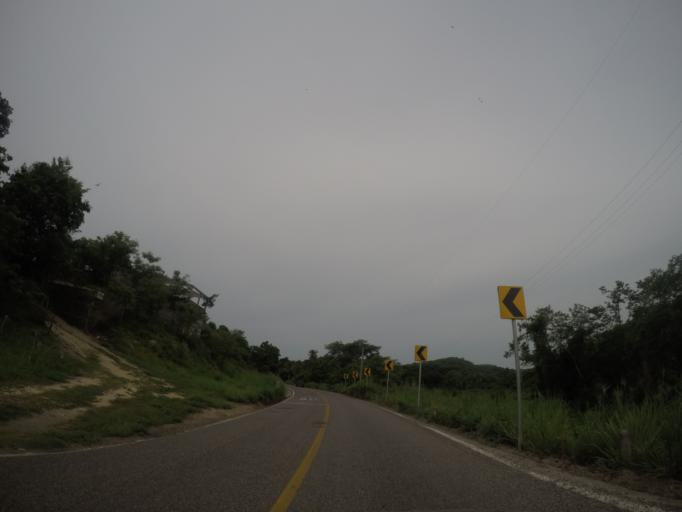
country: MX
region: Oaxaca
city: San Pedro Mixtepec
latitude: 15.9566
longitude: -97.2182
